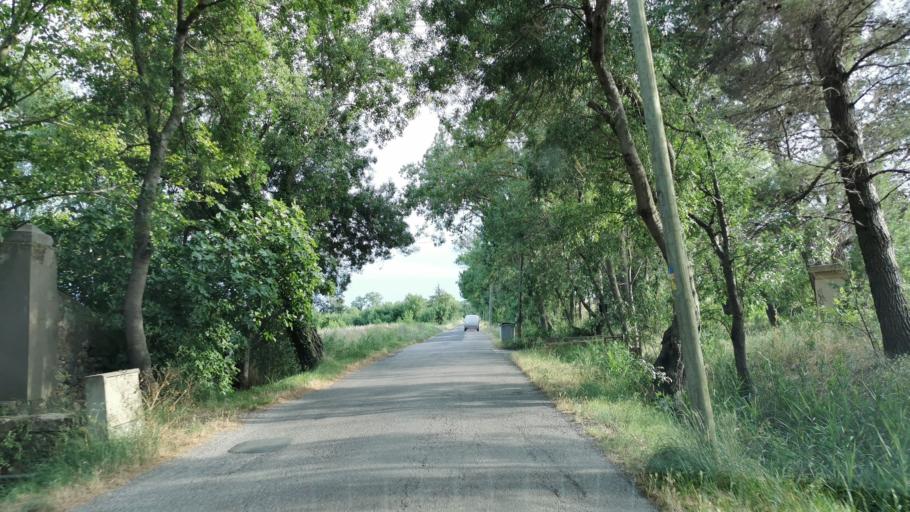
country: FR
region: Languedoc-Roussillon
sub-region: Departement de l'Aude
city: Narbonne
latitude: 43.1976
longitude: 2.9955
